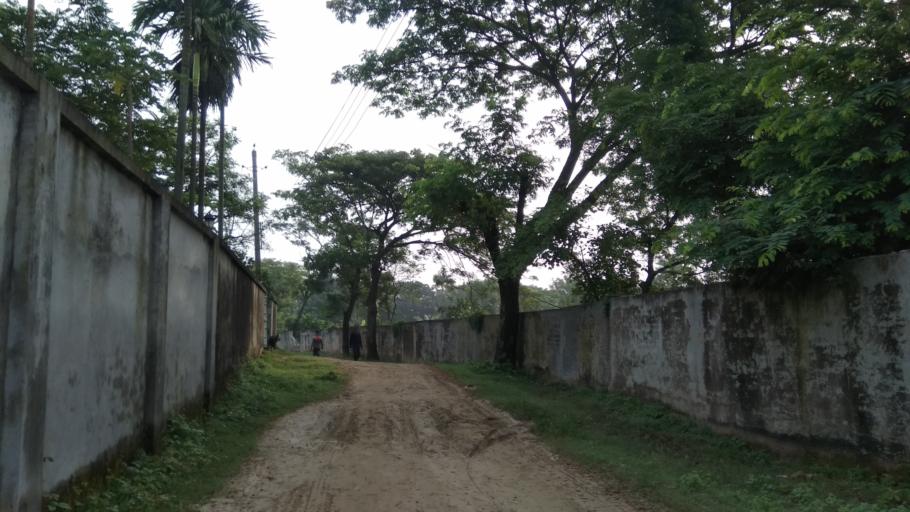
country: BD
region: Dhaka
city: Tungi
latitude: 23.8521
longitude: 90.4408
